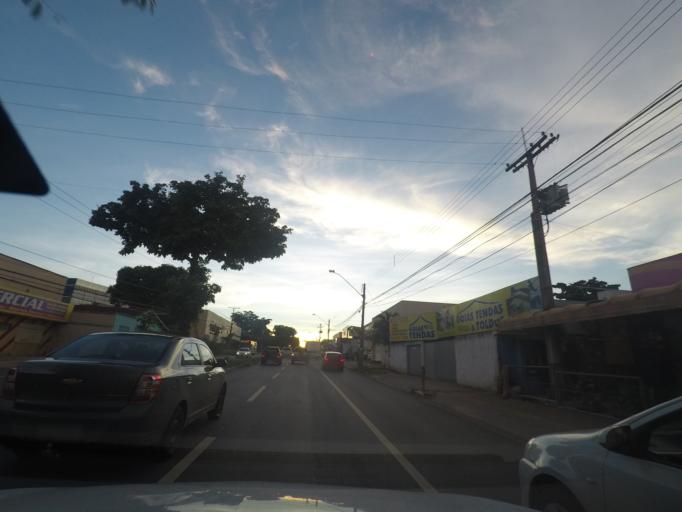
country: BR
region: Goias
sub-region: Goiania
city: Goiania
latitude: -16.6956
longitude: -49.2977
